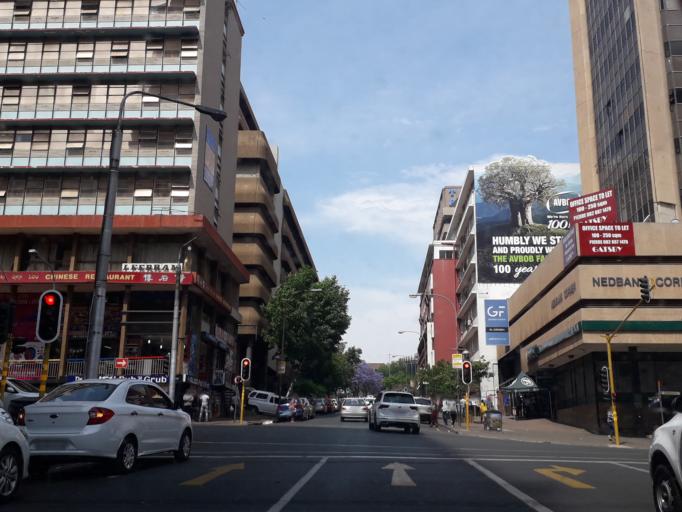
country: ZA
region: Gauteng
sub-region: City of Johannesburg Metropolitan Municipality
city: Johannesburg
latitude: -26.1927
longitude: 28.0366
